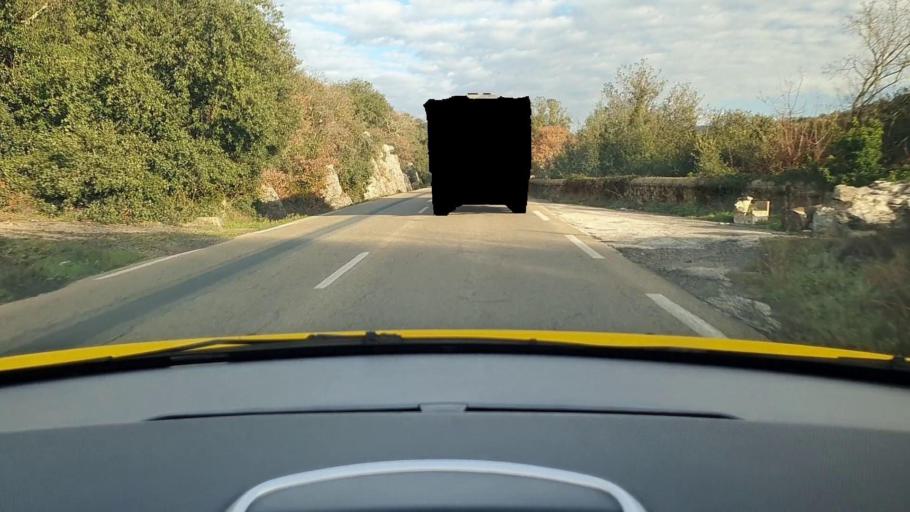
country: FR
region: Languedoc-Roussillon
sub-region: Departement du Gard
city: Saint-Martin-de-Valgalgues
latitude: 44.1763
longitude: 4.0815
